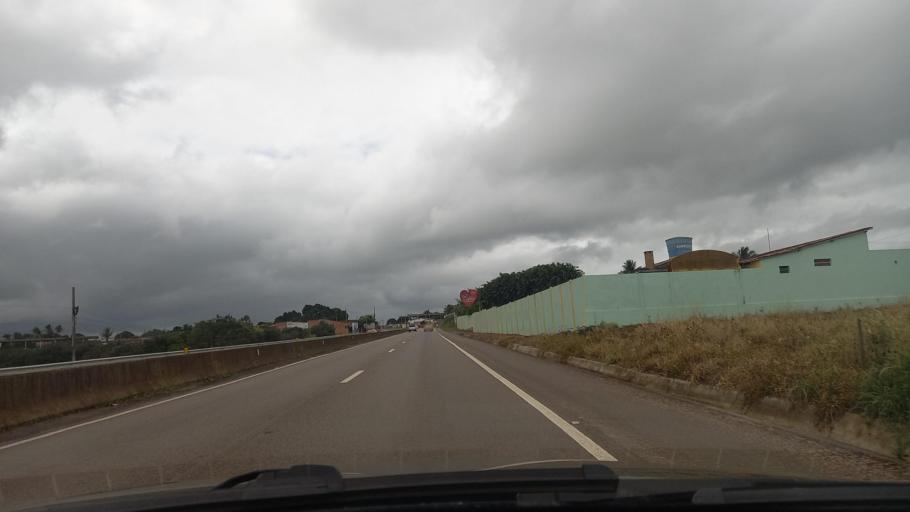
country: BR
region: Alagoas
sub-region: Limoeiro De Anadia
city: Limoeiro de Anadia
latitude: -9.7416
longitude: -36.4761
